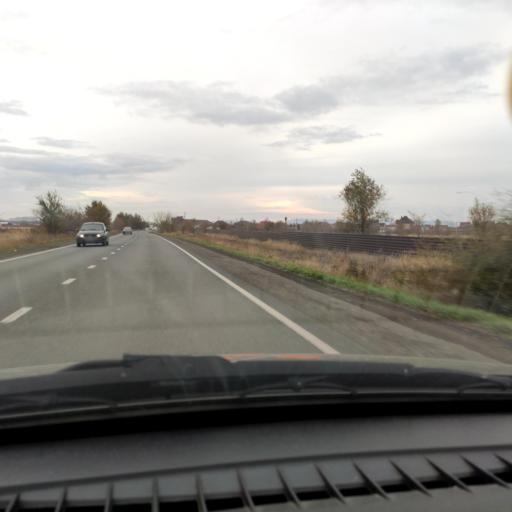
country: RU
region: Samara
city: Podstepki
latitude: 53.5190
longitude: 49.2073
